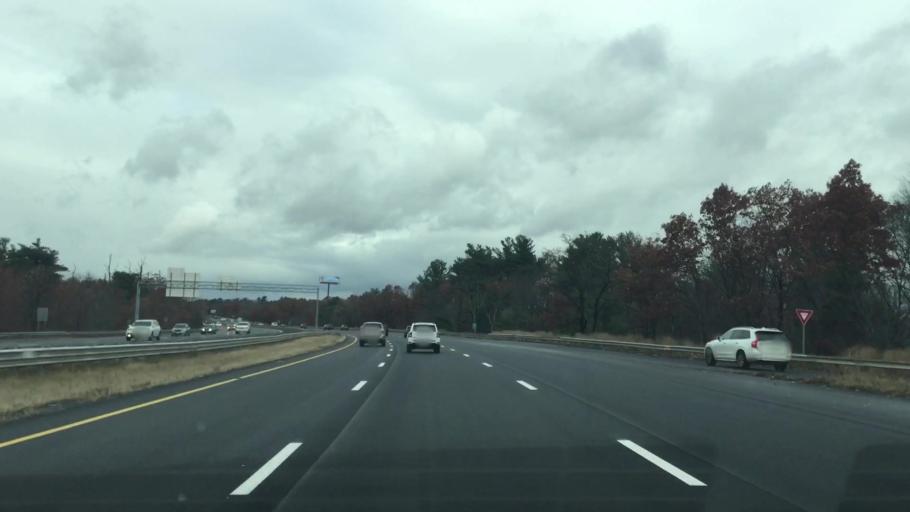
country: US
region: Massachusetts
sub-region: Essex County
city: Methuen
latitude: 42.7371
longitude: -71.2042
